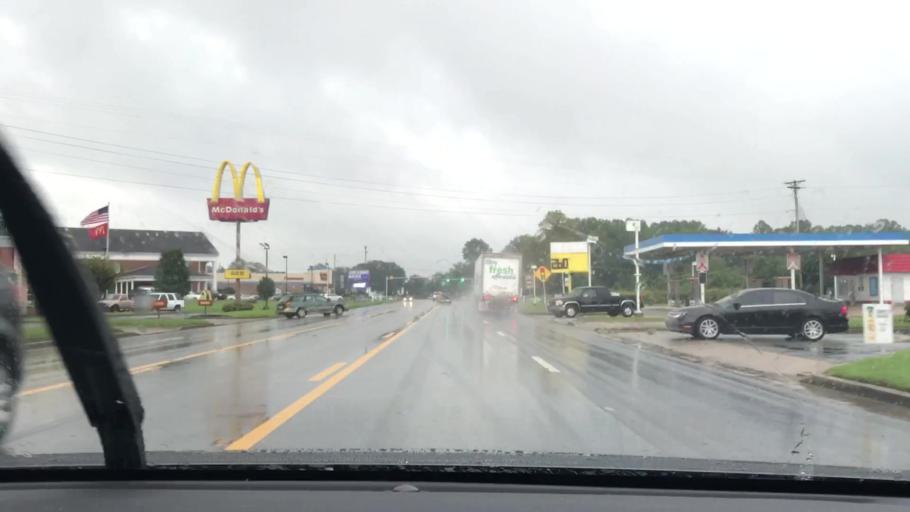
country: US
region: Tennessee
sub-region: Macon County
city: Lafayette
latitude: 36.5205
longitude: -86.0364
